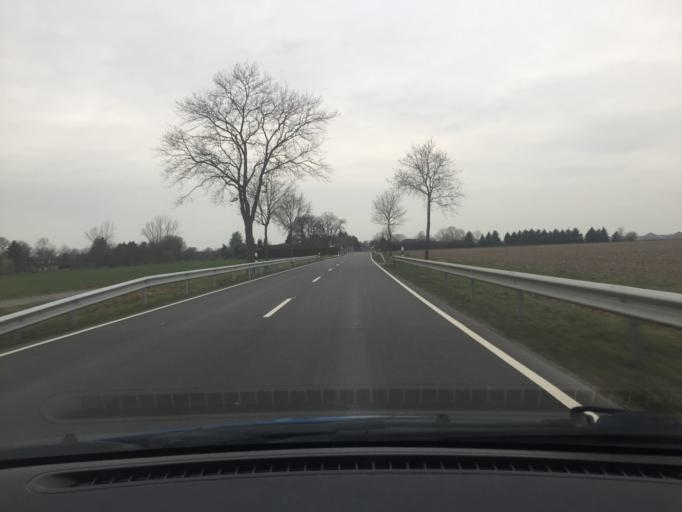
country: DE
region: Lower Saxony
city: Waddeweitz
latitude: 52.9912
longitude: 10.9712
